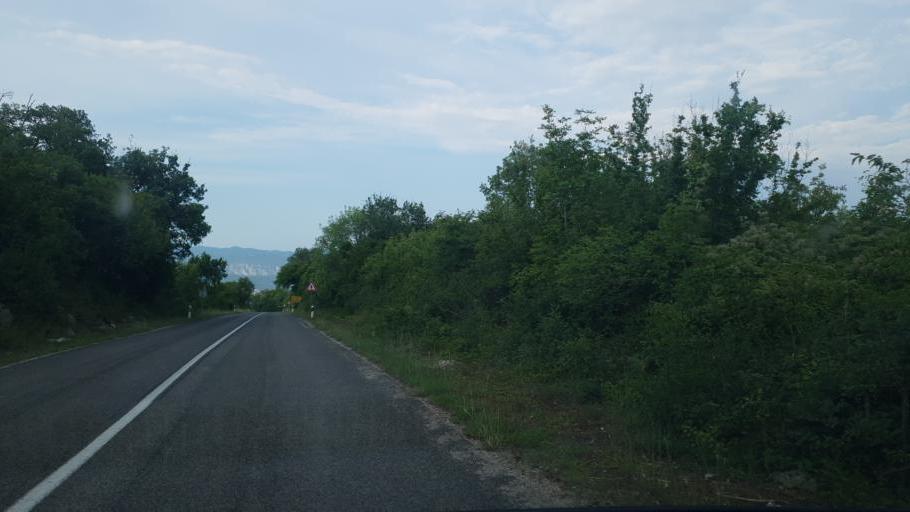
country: HR
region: Primorsko-Goranska
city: Njivice
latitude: 45.1313
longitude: 14.5808
